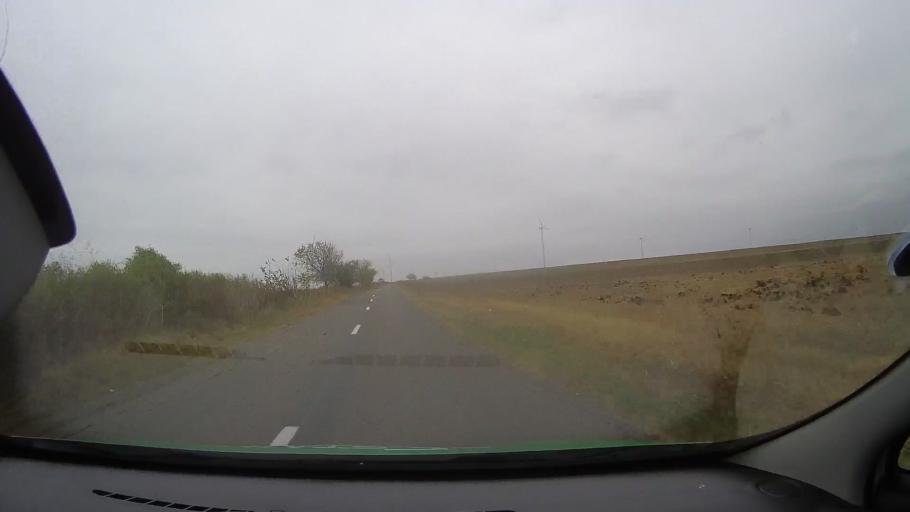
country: RO
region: Constanta
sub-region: Comuna Pantelimon
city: Pantelimon
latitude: 44.5007
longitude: 28.3556
